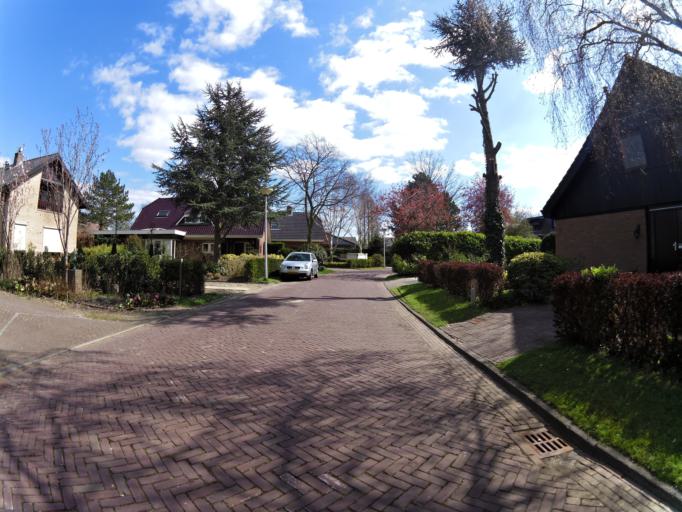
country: NL
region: South Holland
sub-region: Gemeente Brielle
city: Brielle
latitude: 51.8960
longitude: 4.1642
